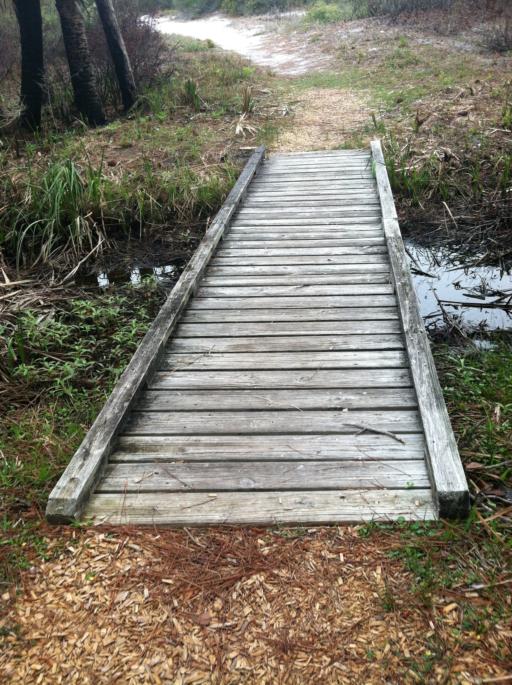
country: US
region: Florida
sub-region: Gulf County
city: Port Saint Joe
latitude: 29.7807
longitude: -85.4074
